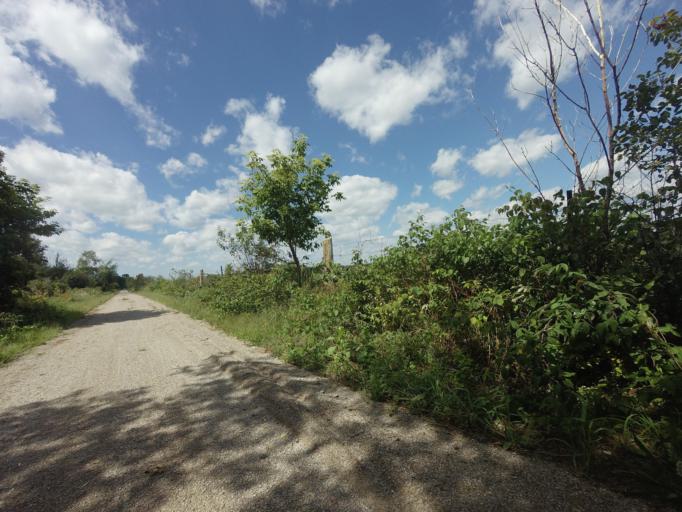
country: CA
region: Ontario
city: Huron East
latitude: 43.6361
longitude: -81.1924
